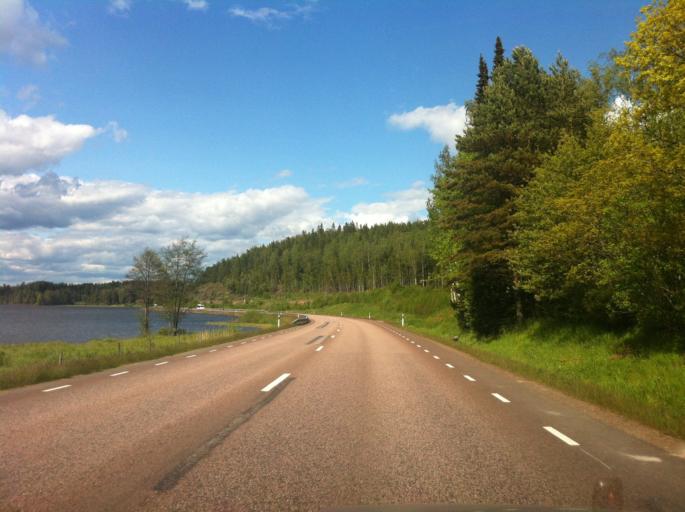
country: SE
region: Vaermland
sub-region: Kristinehamns Kommun
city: Kristinehamn
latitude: 59.3934
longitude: 14.2043
